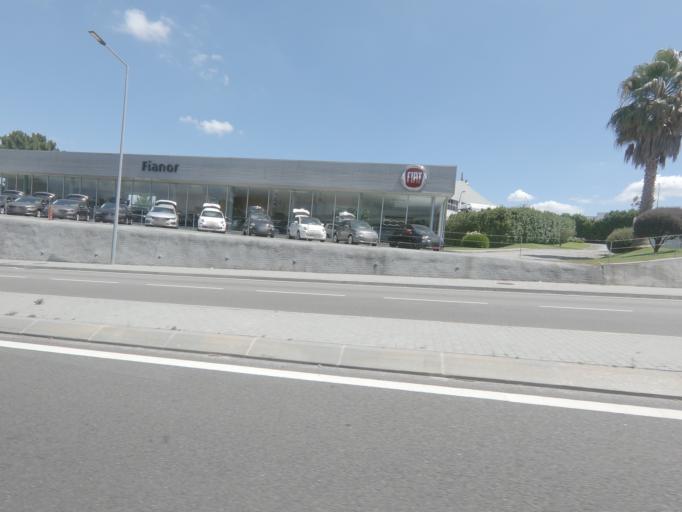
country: PT
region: Porto
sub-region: Paredes
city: Paredes
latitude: 41.1971
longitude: -8.3073
